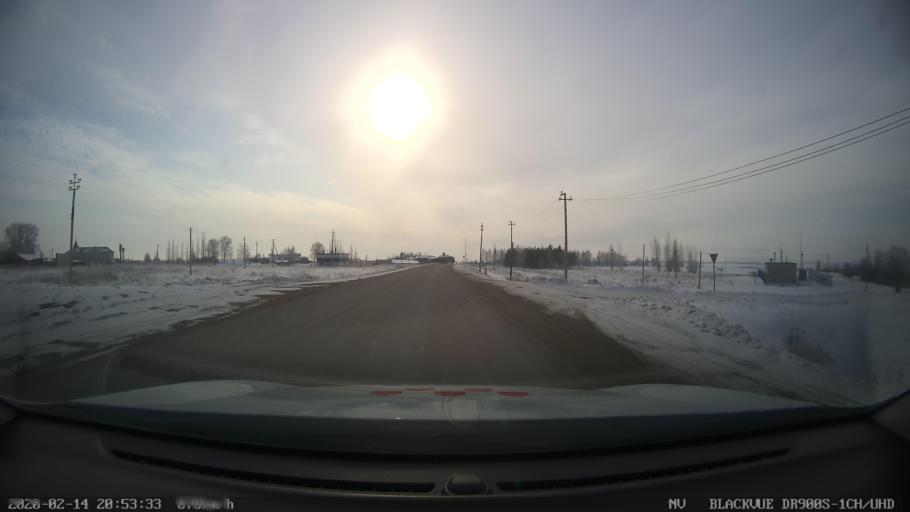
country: RU
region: Tatarstan
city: Kuybyshevskiy Zaton
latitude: 55.1933
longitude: 49.2474
